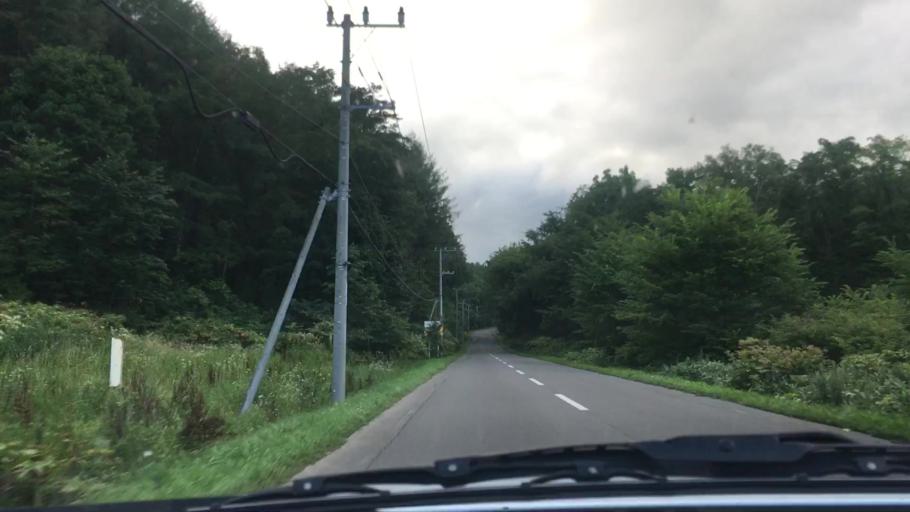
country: JP
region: Hokkaido
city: Otofuke
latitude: 43.1437
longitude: 142.8795
